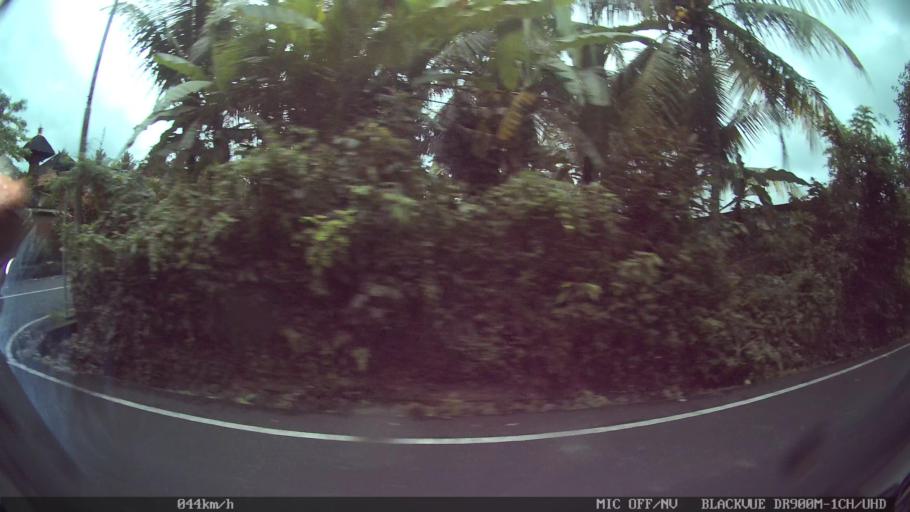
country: ID
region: Bali
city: Banjar Serangan
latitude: -8.5408
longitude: 115.1837
